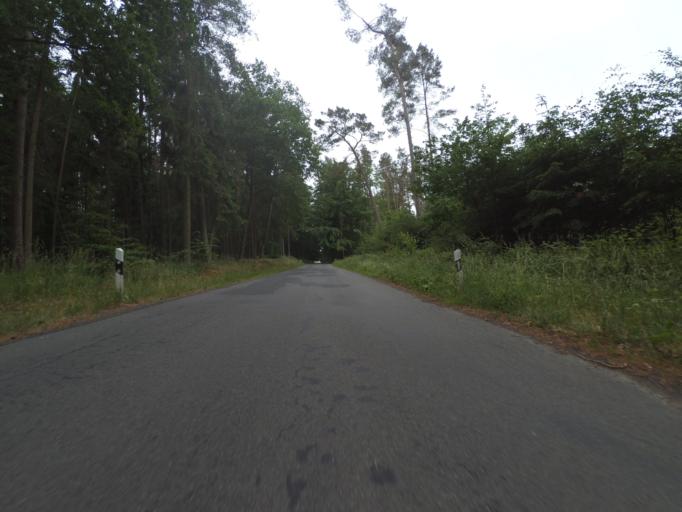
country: DE
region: Mecklenburg-Vorpommern
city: Demen
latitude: 53.6339
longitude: 11.8301
